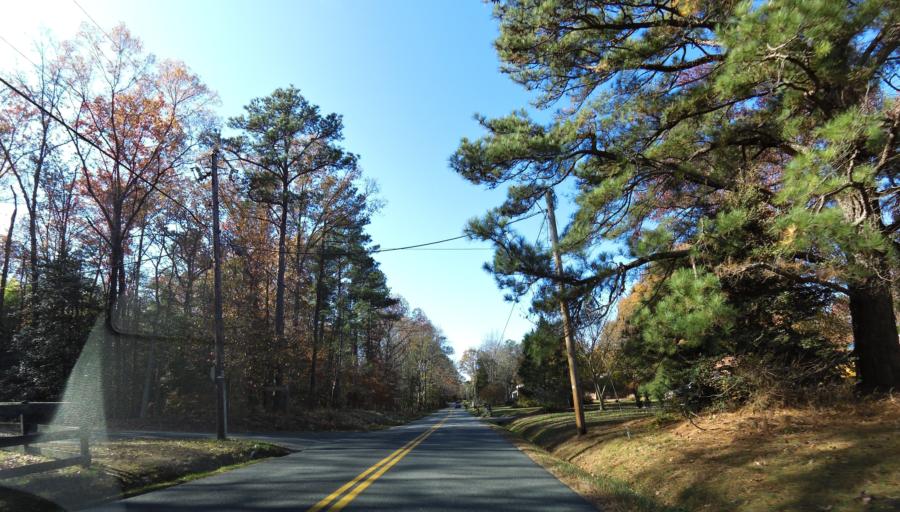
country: US
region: Virginia
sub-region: Hanover County
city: Hanover
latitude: 37.7173
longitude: -77.4060
